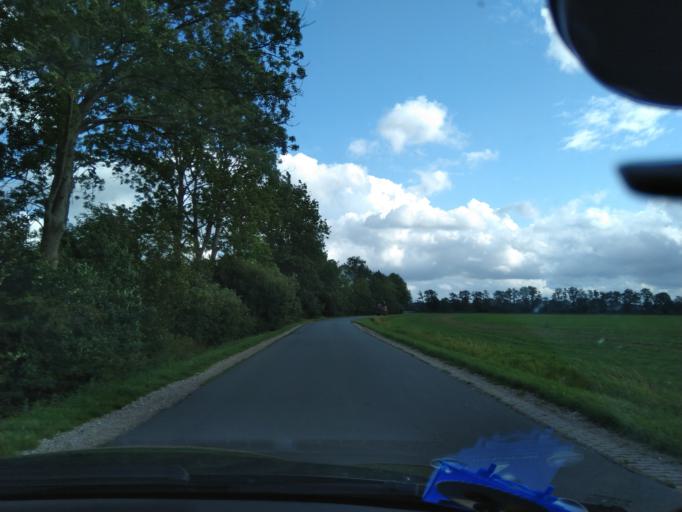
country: NL
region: Drenthe
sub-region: Gemeente Tynaarlo
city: Vries
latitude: 53.0899
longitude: 6.5348
